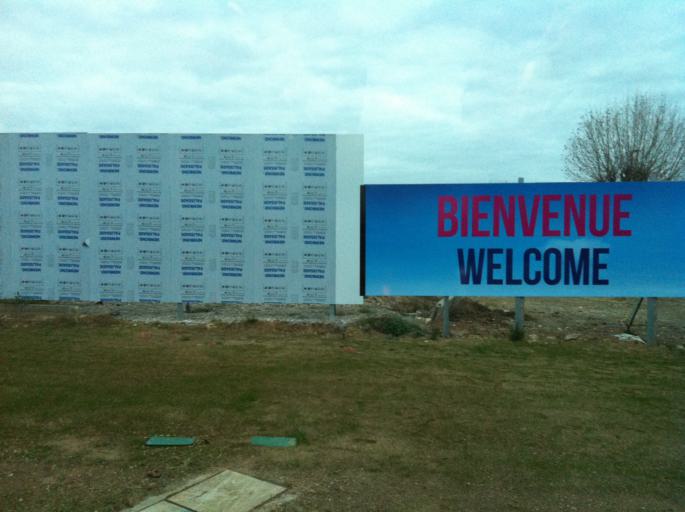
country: FR
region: Languedoc-Roussillon
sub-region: Departement de l'Herault
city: Perols
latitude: 43.5798
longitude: 3.9519
